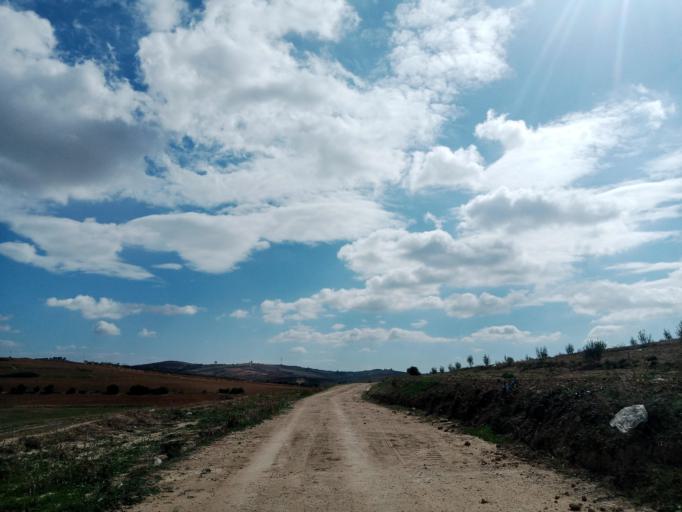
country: TN
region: Tunis
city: Oued Lill
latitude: 36.8091
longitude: 9.9837
